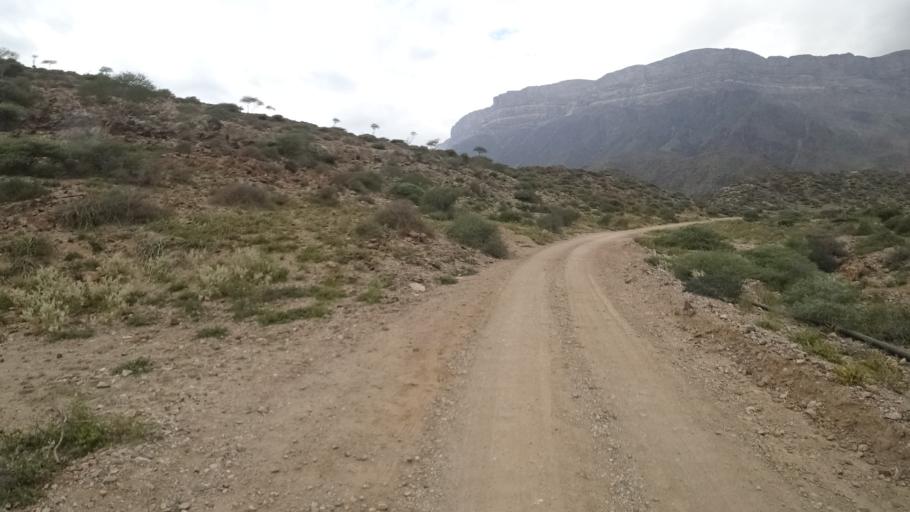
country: OM
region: Zufar
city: Salalah
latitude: 17.1713
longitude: 54.9532
